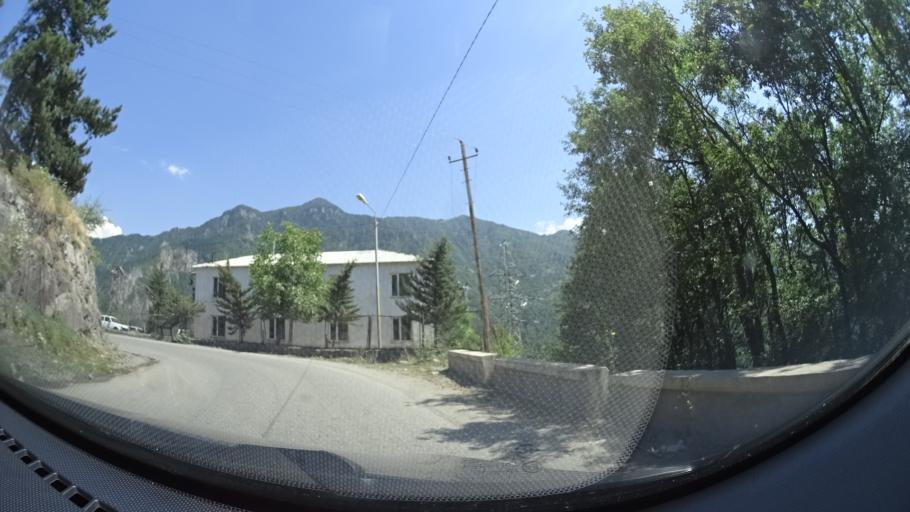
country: GE
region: Ajaria
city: Khulo
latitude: 41.6399
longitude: 42.3071
